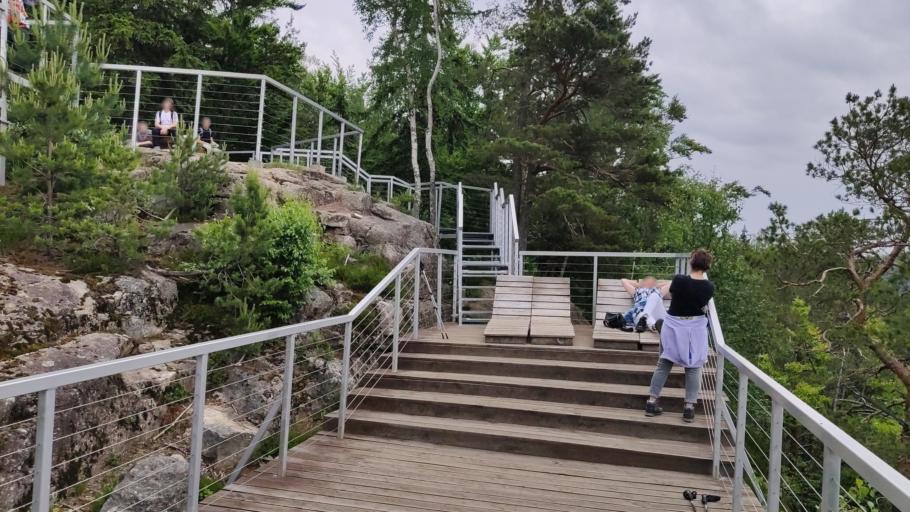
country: PL
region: Lower Silesian Voivodeship
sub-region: Powiat jeleniogorski
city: Szklarska Poreba
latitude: 50.8323
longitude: 15.5530
